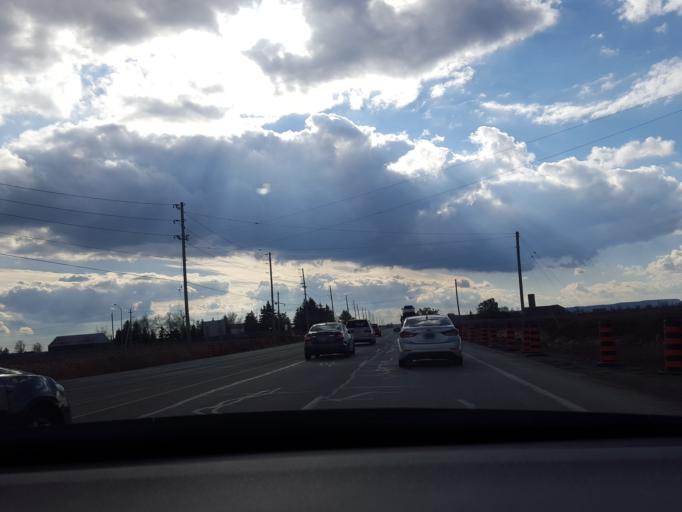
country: CA
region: Ontario
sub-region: Halton
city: Milton
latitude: 43.5697
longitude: -79.7923
